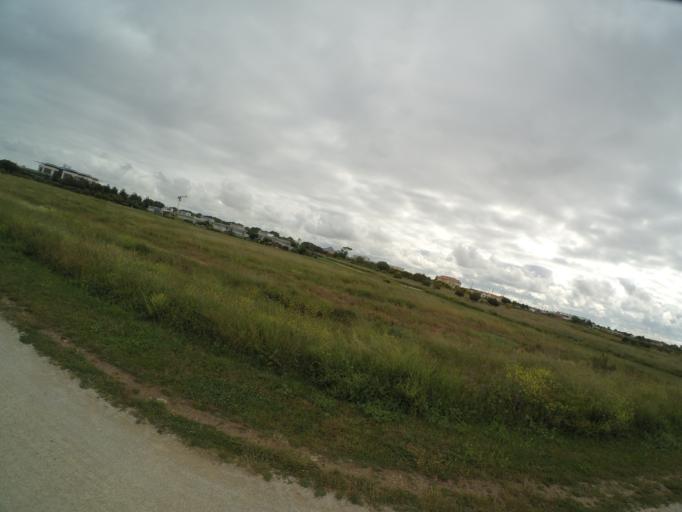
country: FR
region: Poitou-Charentes
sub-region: Departement de la Charente-Maritime
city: La Rochelle
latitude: 46.1341
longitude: -1.1507
